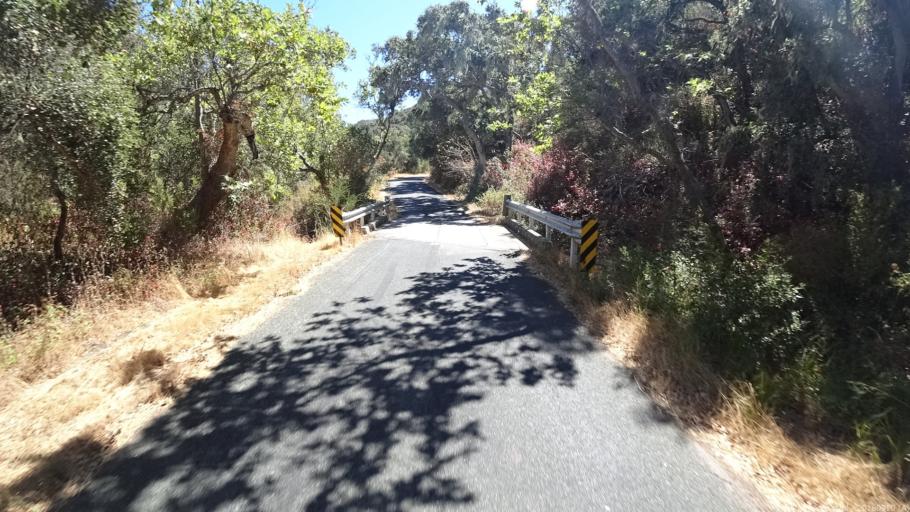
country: US
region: California
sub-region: Monterey County
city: Carmel Valley Village
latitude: 36.4889
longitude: -121.8100
